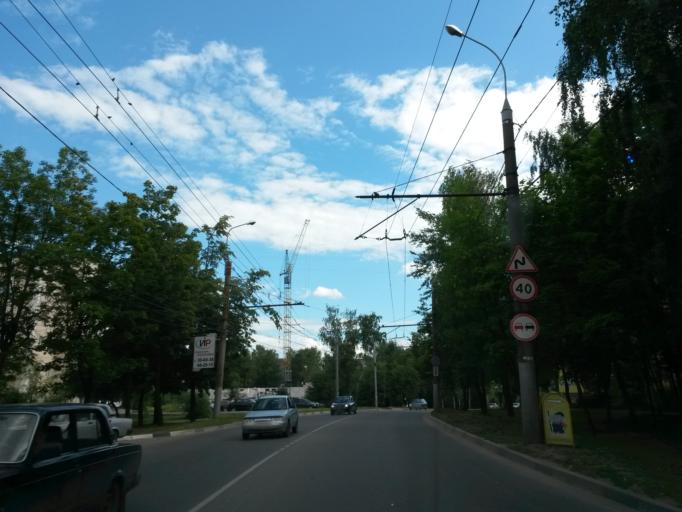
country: RU
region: Ivanovo
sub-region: Gorod Ivanovo
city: Ivanovo
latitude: 56.9853
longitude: 40.9927
